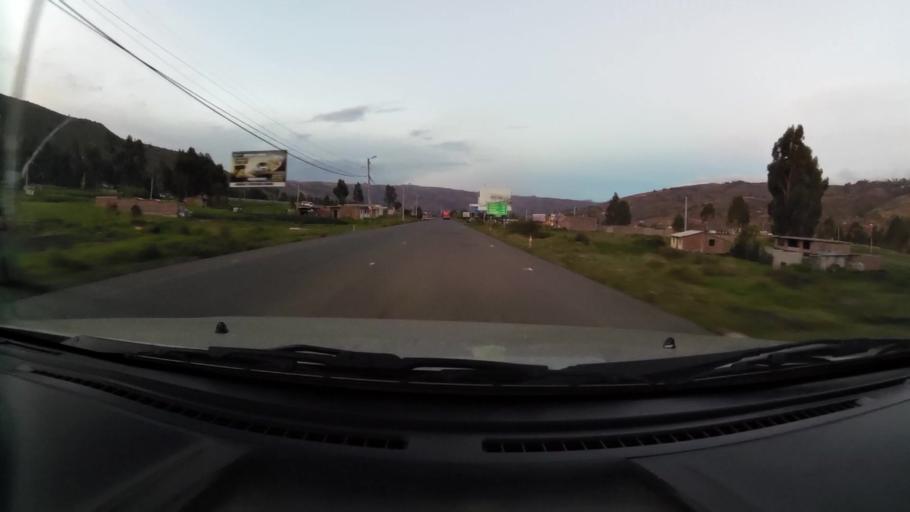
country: EC
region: Chimborazo
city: Riobamba
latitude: -1.9224
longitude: -78.7016
